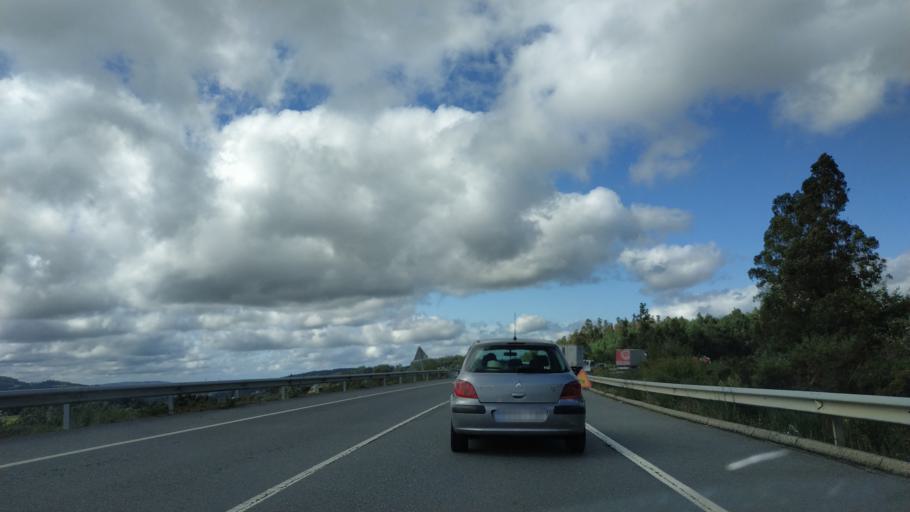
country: ES
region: Galicia
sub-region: Provincia da Coruna
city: Cerceda
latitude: 43.2288
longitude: -8.4670
